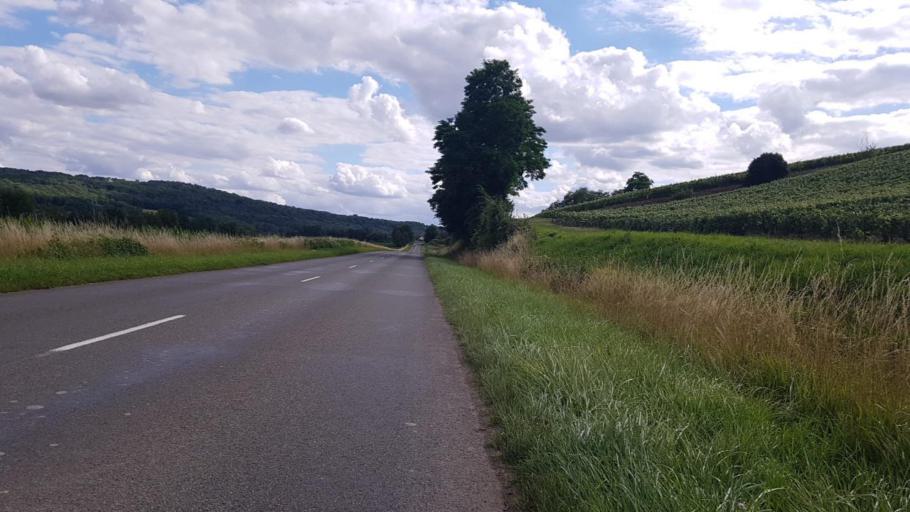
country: FR
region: Picardie
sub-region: Departement de l'Aisne
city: Crezancy
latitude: 49.0589
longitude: 3.4753
